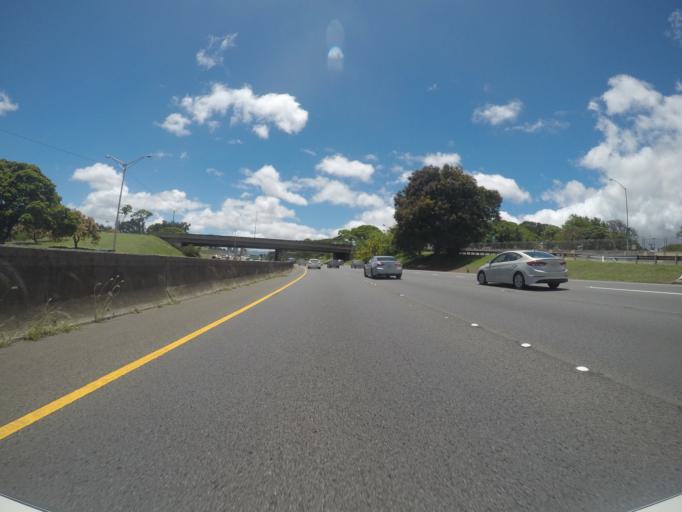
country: US
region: Hawaii
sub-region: Honolulu County
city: Halawa Heights
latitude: 21.3422
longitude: -157.8872
